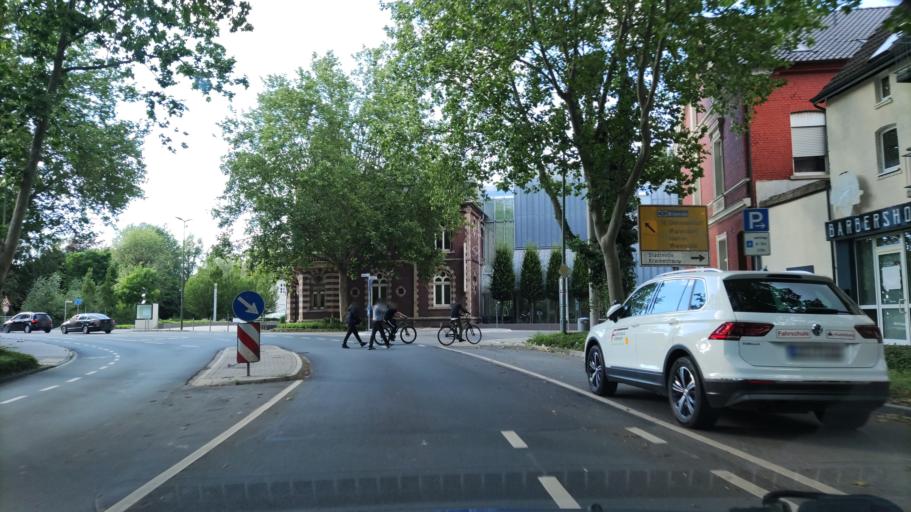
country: DE
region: North Rhine-Westphalia
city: Ahlen
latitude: 51.7627
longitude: 7.8860
